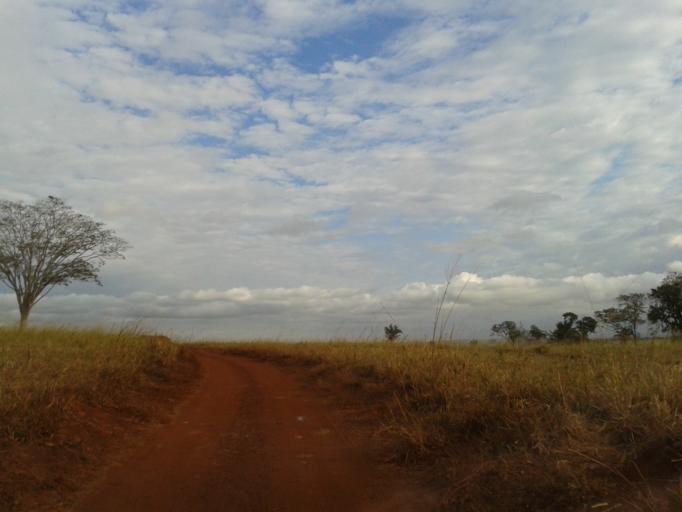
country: BR
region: Minas Gerais
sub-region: Santa Vitoria
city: Santa Vitoria
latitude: -18.7340
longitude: -50.2247
